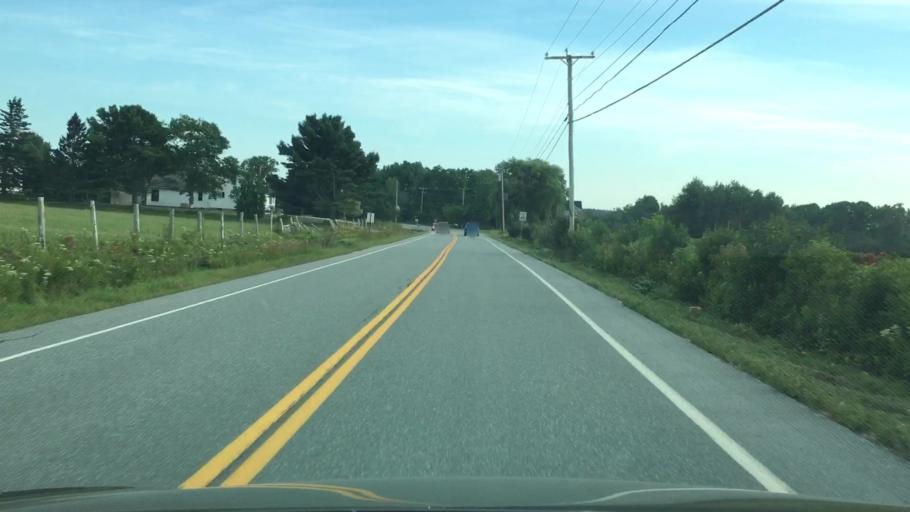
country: US
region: Maine
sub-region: Hancock County
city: Penobscot
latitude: 44.4643
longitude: -68.7825
